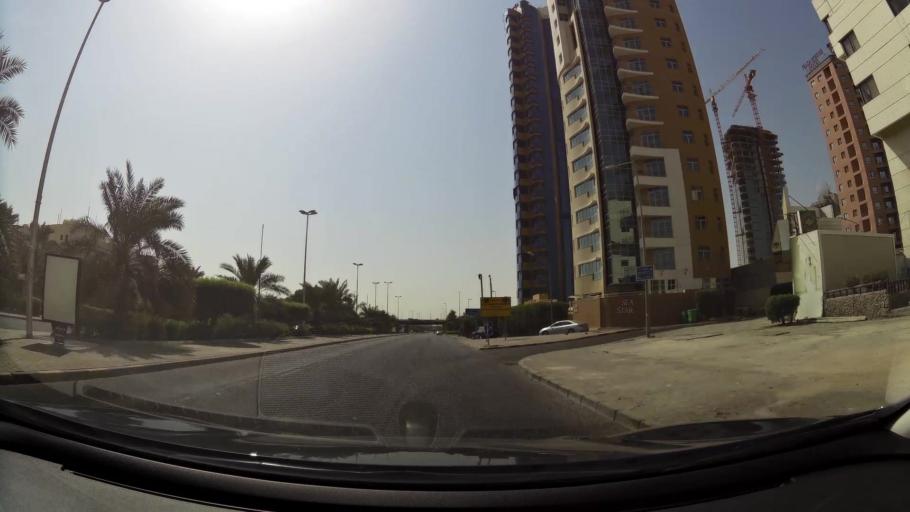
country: KW
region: Al Asimah
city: Ad Dasmah
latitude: 29.3678
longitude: 48.0121
